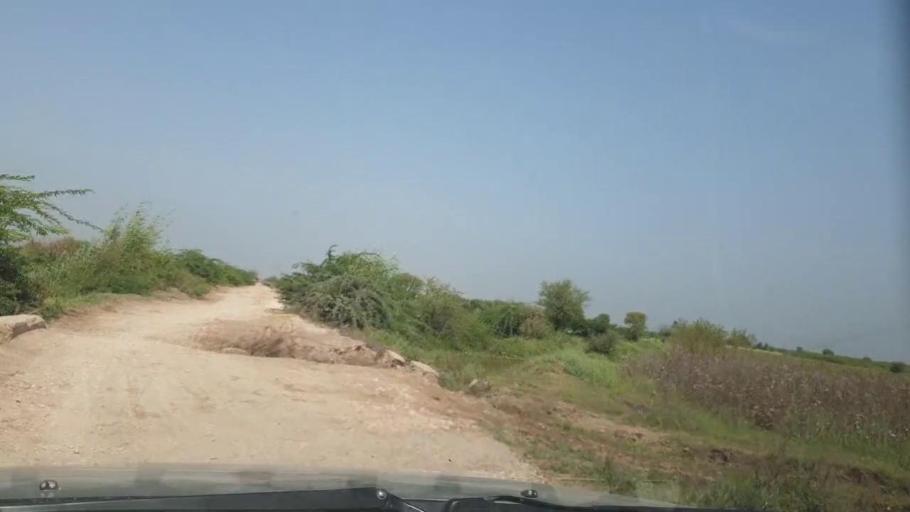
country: PK
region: Sindh
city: Tando Ghulam Ali
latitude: 25.0891
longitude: 68.8021
